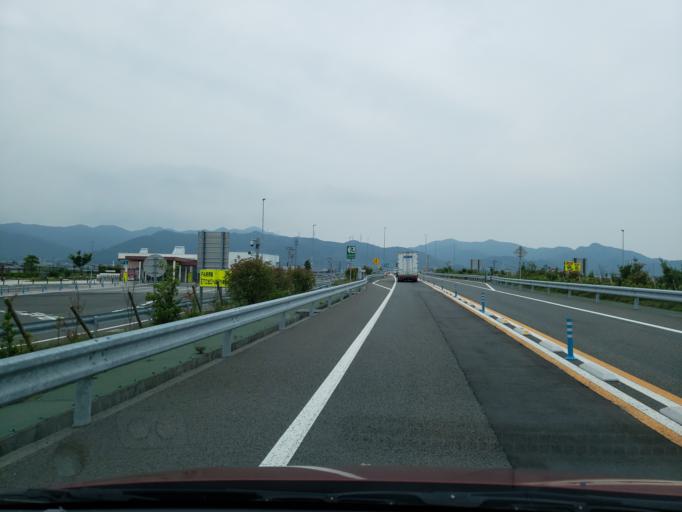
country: JP
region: Tokushima
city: Narutocho-mitsuishi
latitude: 34.1434
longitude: 134.5645
